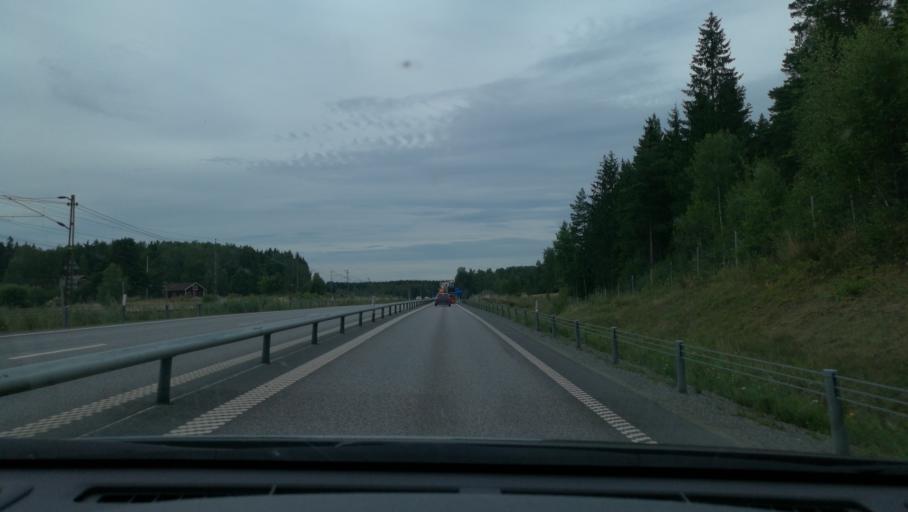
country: SE
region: Soedermanland
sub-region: Katrineholms Kommun
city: Katrineholm
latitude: 58.9252
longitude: 16.1961
